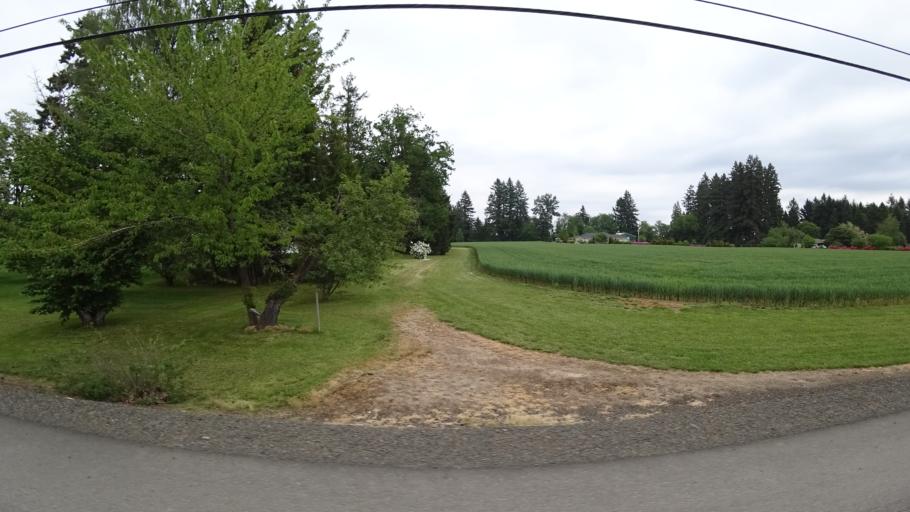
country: US
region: Oregon
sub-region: Washington County
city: Hillsboro
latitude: 45.4923
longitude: -122.9910
